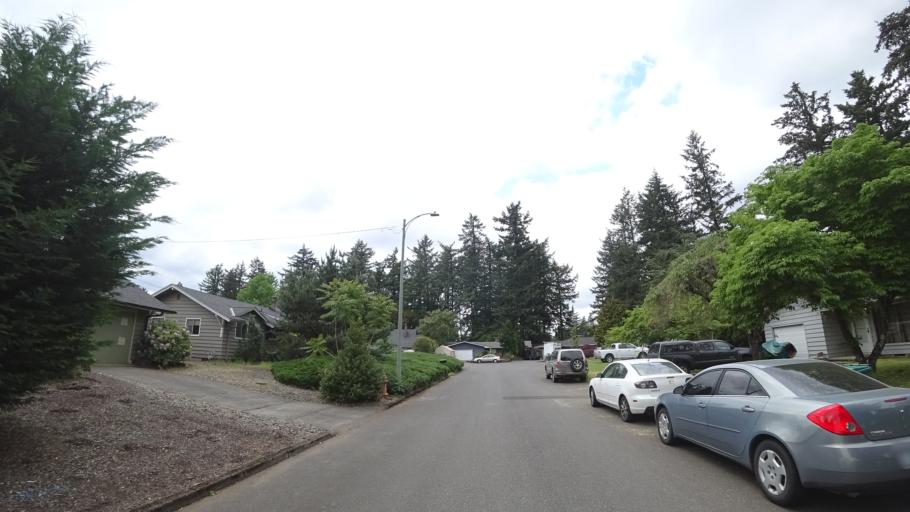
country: US
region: Oregon
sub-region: Multnomah County
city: Lents
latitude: 45.5056
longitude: -122.5442
